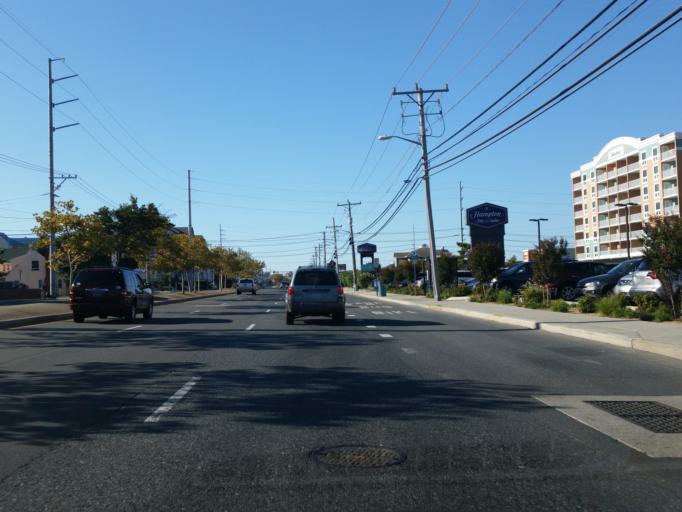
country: US
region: Maryland
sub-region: Worcester County
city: Ocean City
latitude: 38.3704
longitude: -75.0708
